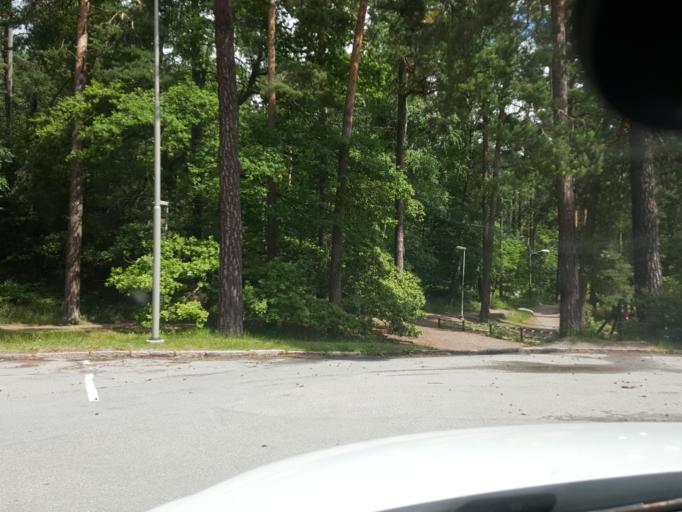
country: SE
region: Stockholm
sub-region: Stockholms Kommun
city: Bromma
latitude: 59.3157
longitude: 17.9650
